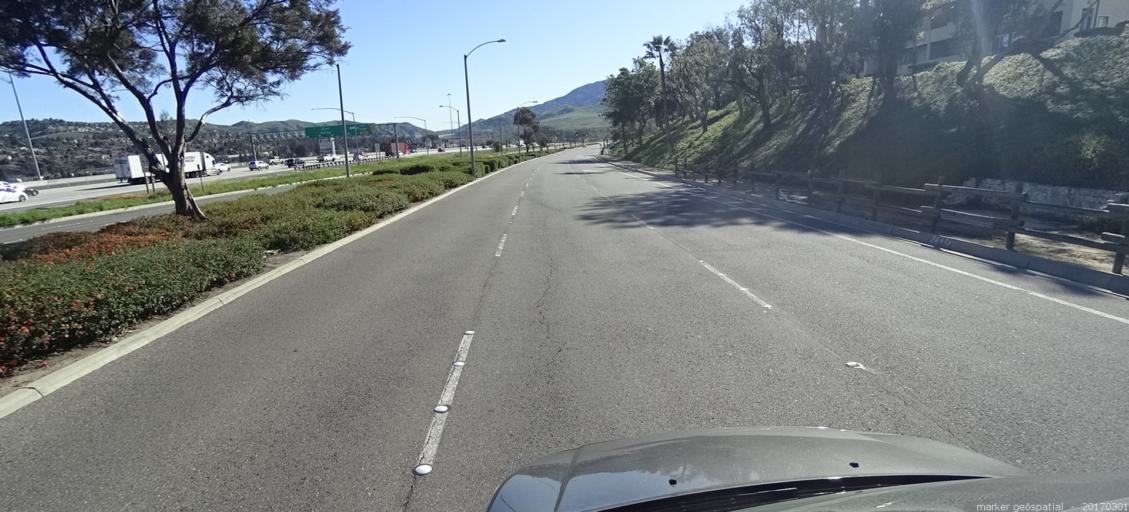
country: US
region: California
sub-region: Orange County
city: Yorba Linda
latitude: 33.8702
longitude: -117.7379
